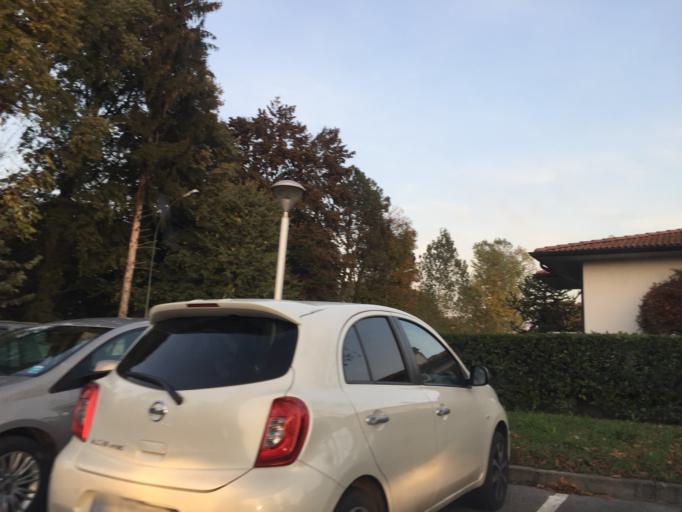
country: IT
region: Lombardy
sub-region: Provincia di Brescia
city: Flero
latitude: 45.4814
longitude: 10.1770
